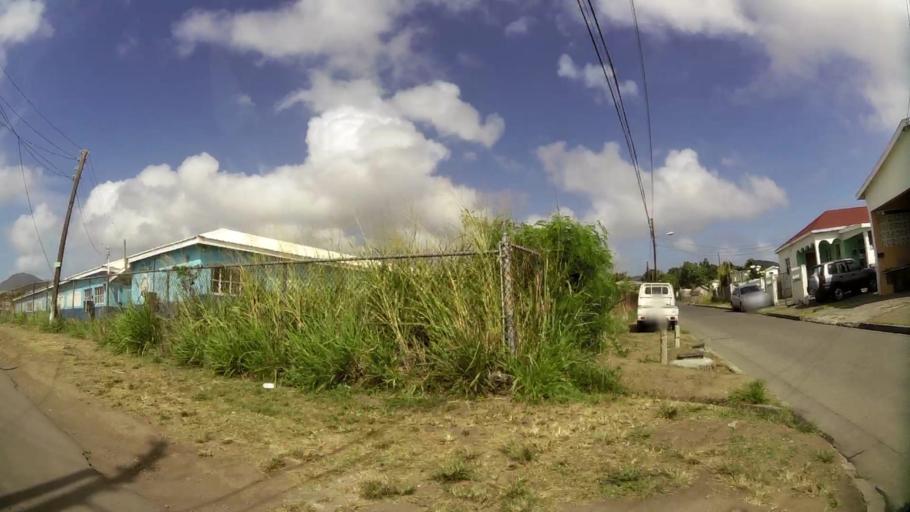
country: KN
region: Saint George Basseterre
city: Basseterre
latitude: 17.3030
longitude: -62.7210
